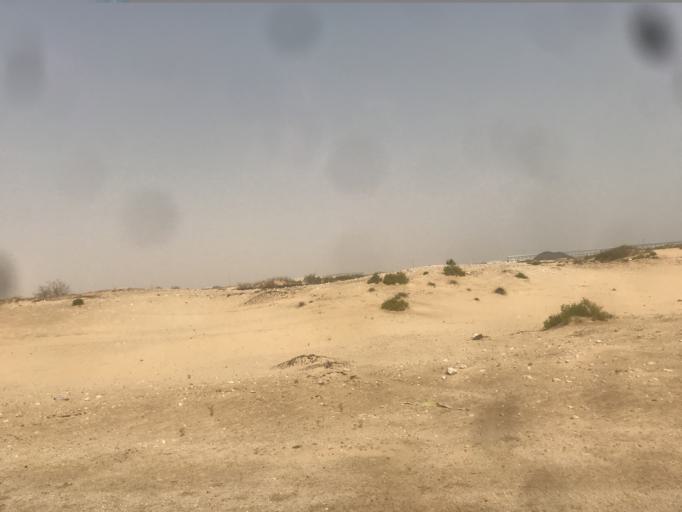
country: SA
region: Eastern Province
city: Abqaiq
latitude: 25.9097
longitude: 49.9405
